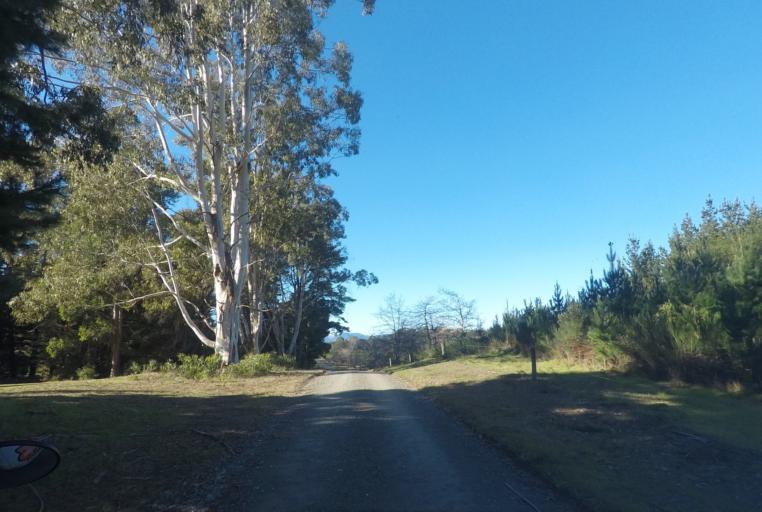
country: NZ
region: Tasman
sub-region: Tasman District
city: Mapua
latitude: -41.2651
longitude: 173.1438
